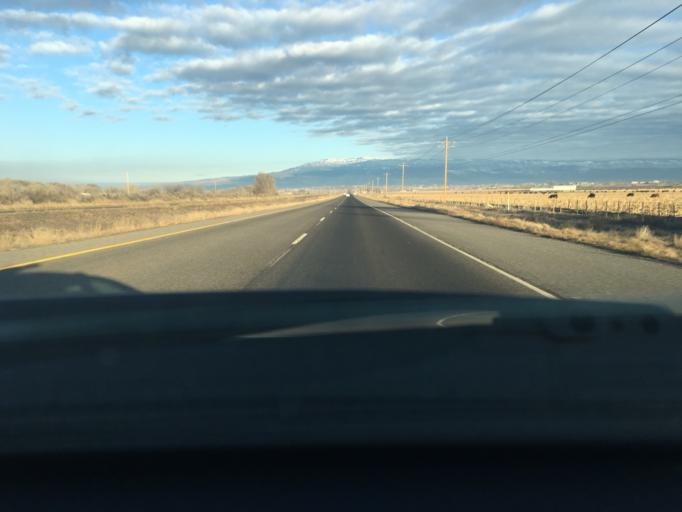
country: US
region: Colorado
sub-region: Montrose County
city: Olathe
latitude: 38.6750
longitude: -108.0035
